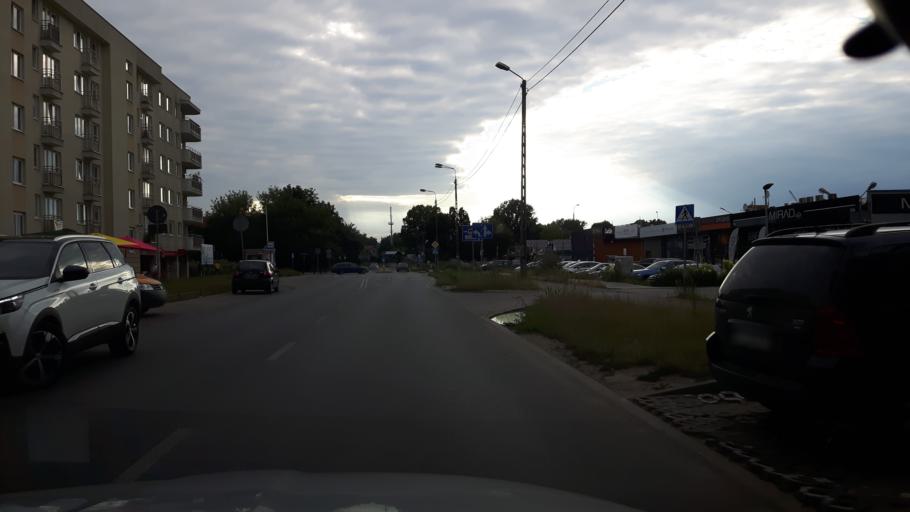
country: PL
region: Masovian Voivodeship
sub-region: Warszawa
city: Mokotow
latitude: 52.2126
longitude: 21.0602
